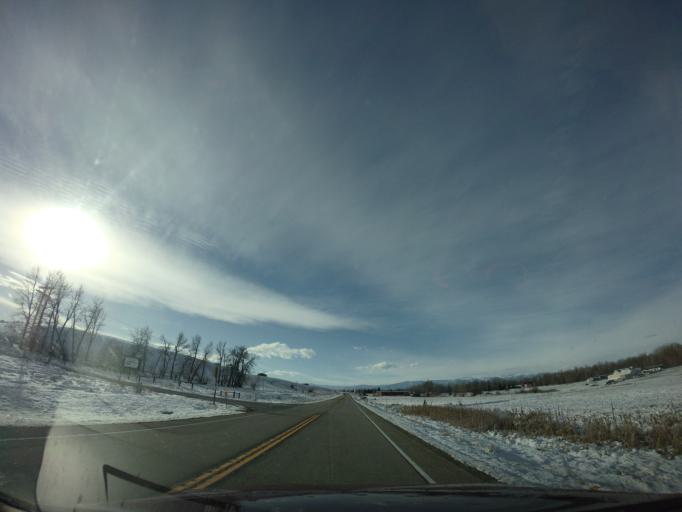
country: US
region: Montana
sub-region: Carbon County
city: Red Lodge
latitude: 45.3929
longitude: -109.1321
